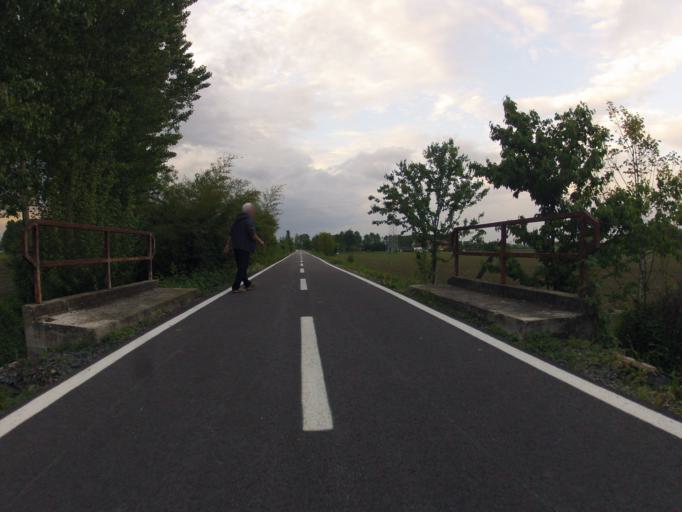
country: IT
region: Piedmont
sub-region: Provincia di Torino
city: Vigone
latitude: 44.8513
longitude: 7.4924
